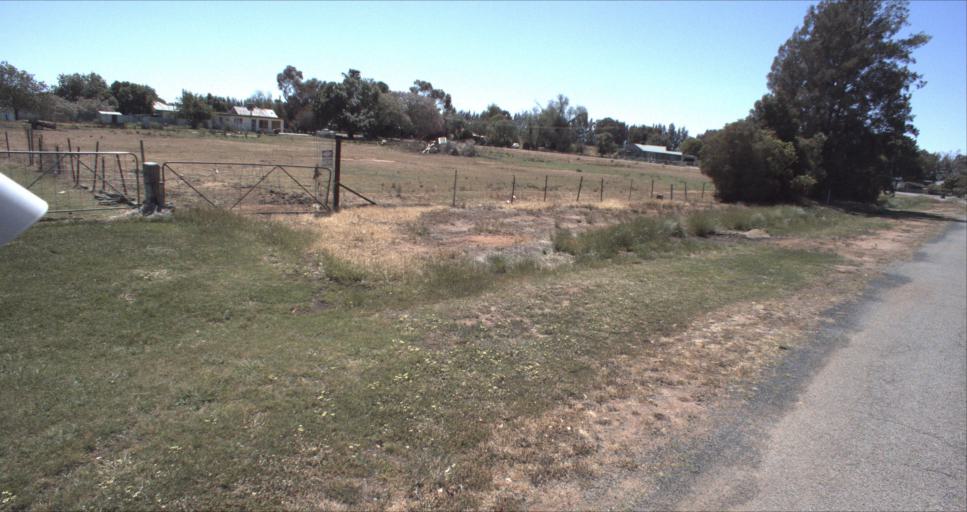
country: AU
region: New South Wales
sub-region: Leeton
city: Leeton
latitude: -34.5250
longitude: 146.3333
